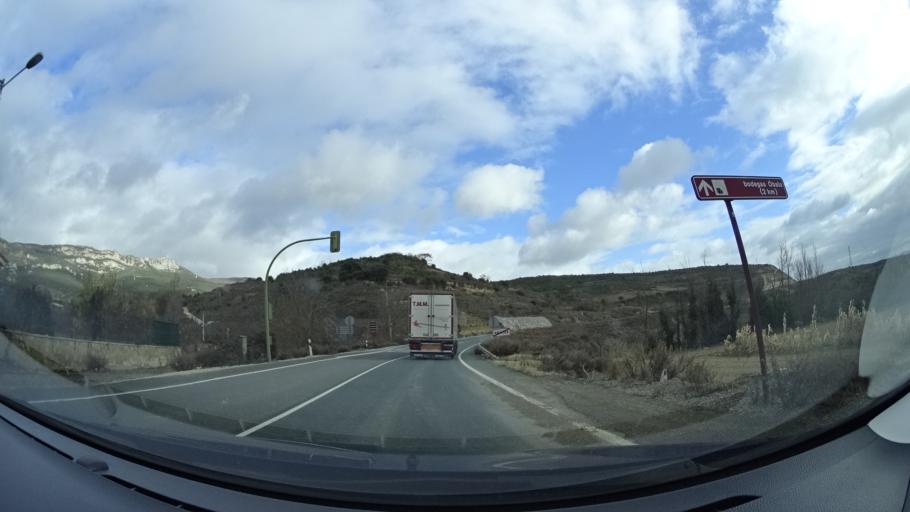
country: ES
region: La Rioja
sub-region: Provincia de La Rioja
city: Abalos
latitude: 42.5716
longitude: -2.7083
